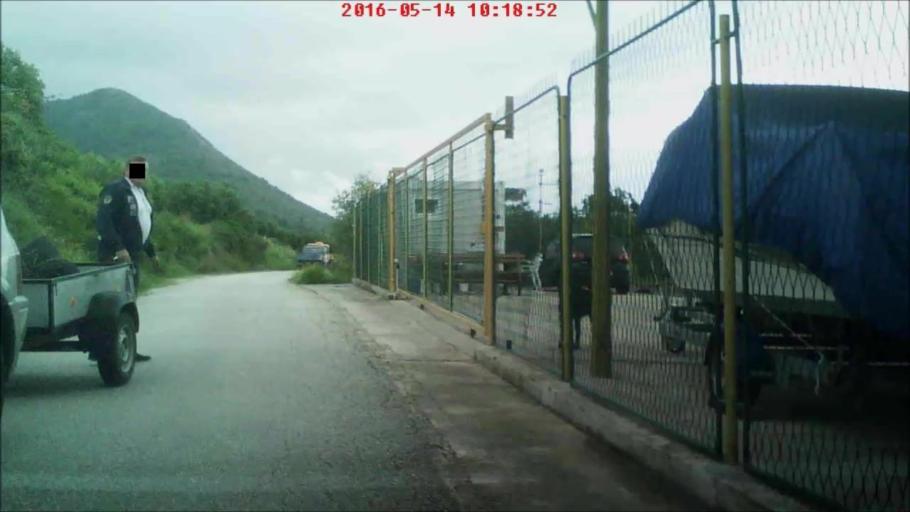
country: HR
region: Dubrovacko-Neretvanska
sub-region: Grad Dubrovnik
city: Mokosica
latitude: 42.7177
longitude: 17.9688
